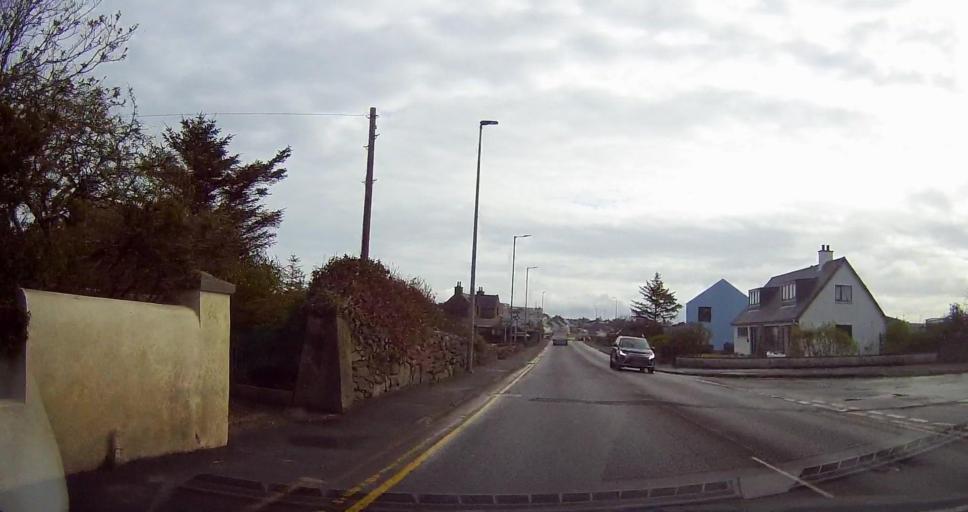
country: GB
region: Scotland
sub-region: Shetland Islands
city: Lerwick
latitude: 60.1477
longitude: -1.1642
